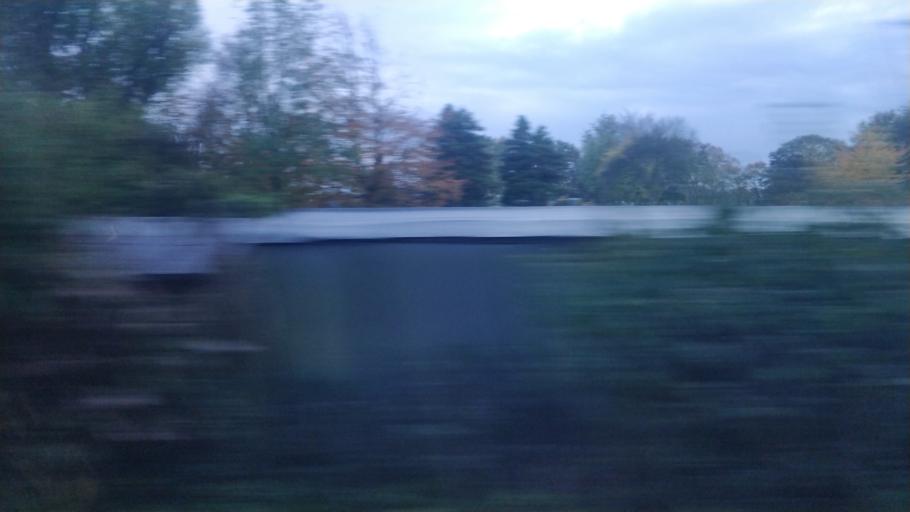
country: GB
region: England
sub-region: Lancashire
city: Parbold
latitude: 53.5999
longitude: -2.8142
